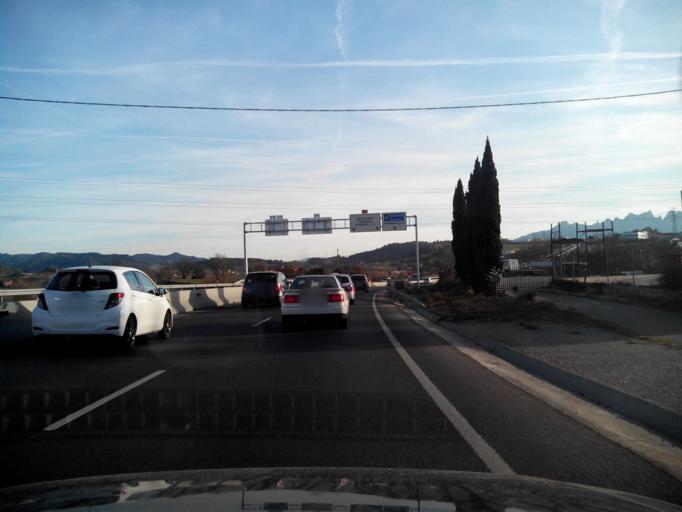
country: ES
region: Catalonia
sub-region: Provincia de Barcelona
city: Sant Fruitos de Bages
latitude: 41.7329
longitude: 1.8516
